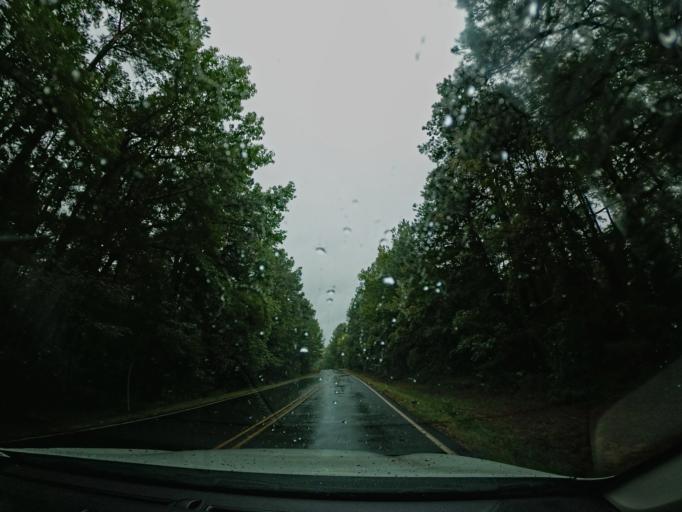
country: US
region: Louisiana
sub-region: Webster Parish
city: Minden
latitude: 32.6540
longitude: -93.2688
